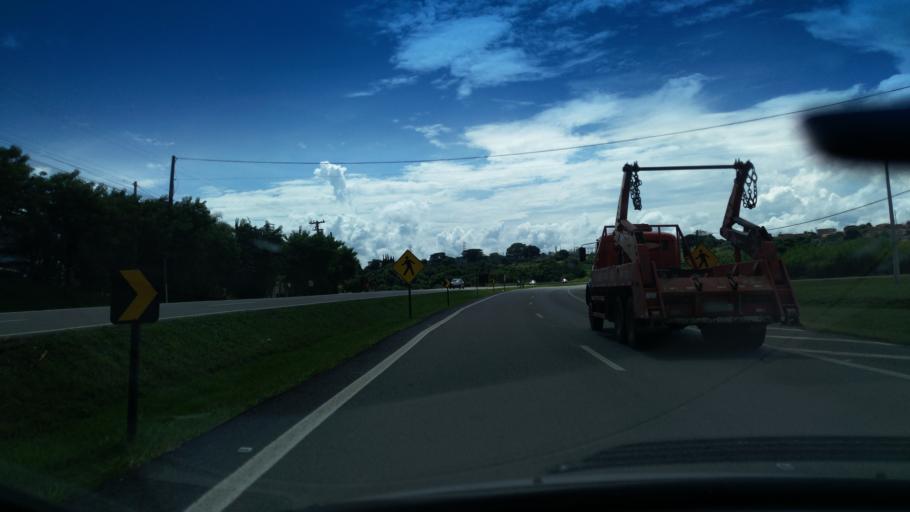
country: BR
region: Sao Paulo
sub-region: Santo Antonio Do Jardim
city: Espirito Santo do Pinhal
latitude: -22.1984
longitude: -46.7769
